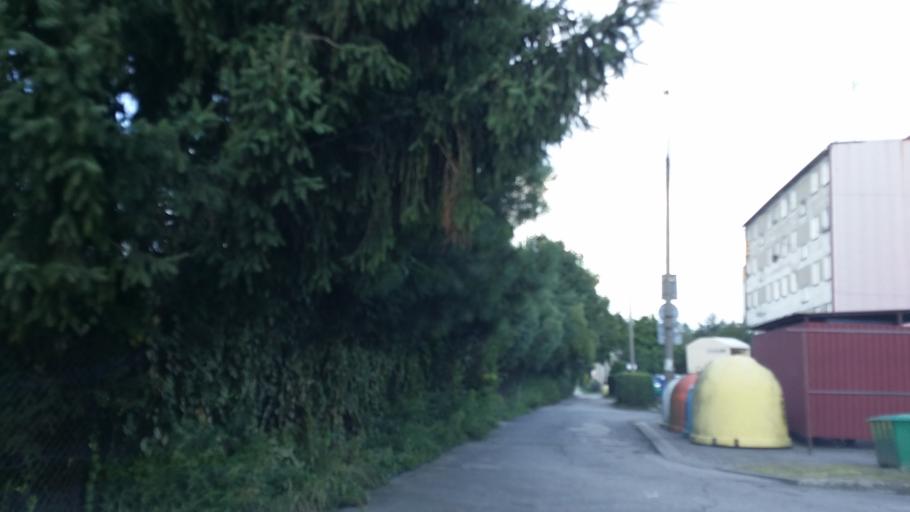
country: PL
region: Lesser Poland Voivodeship
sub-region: Powiat oswiecimski
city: Zator
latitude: 49.9993
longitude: 19.4274
